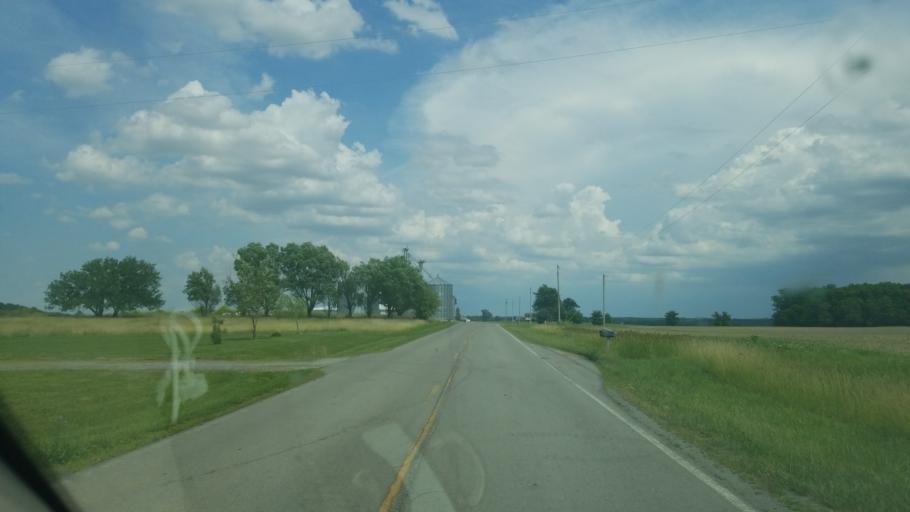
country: US
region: Ohio
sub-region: Hardin County
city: Ada
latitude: 40.6159
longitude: -83.8265
